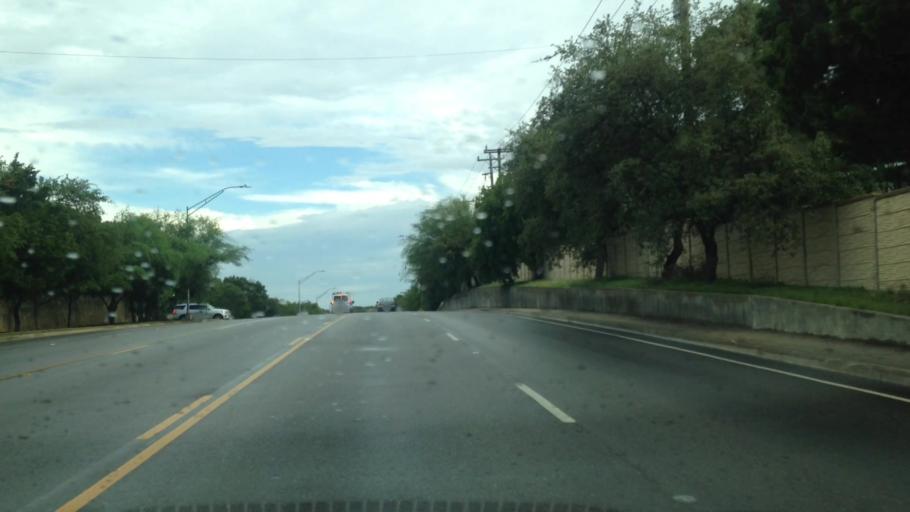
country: US
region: Texas
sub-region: Bexar County
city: Live Oak
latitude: 29.5960
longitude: -98.4028
